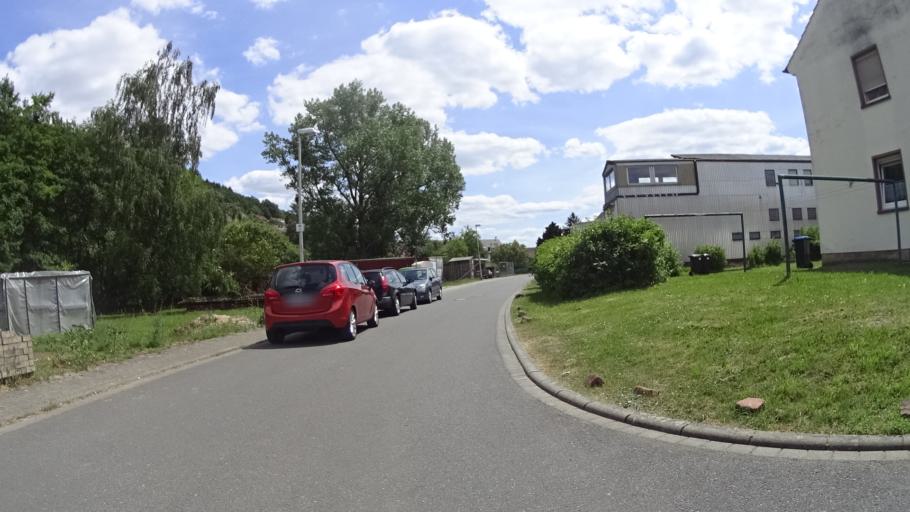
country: DE
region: Bavaria
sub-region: Regierungsbezirk Unterfranken
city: Eichenbuhl
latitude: 49.7063
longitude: 9.3254
